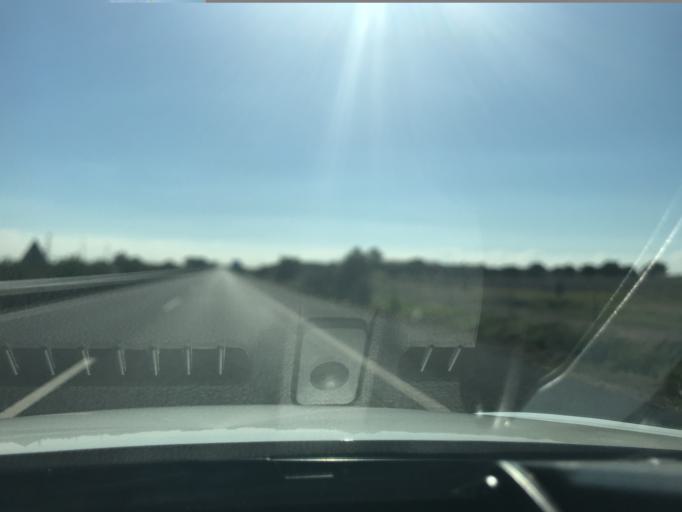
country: ES
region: Andalusia
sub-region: Provincia de Sevilla
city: Fuentes de Andalucia
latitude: 37.5075
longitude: -5.3896
